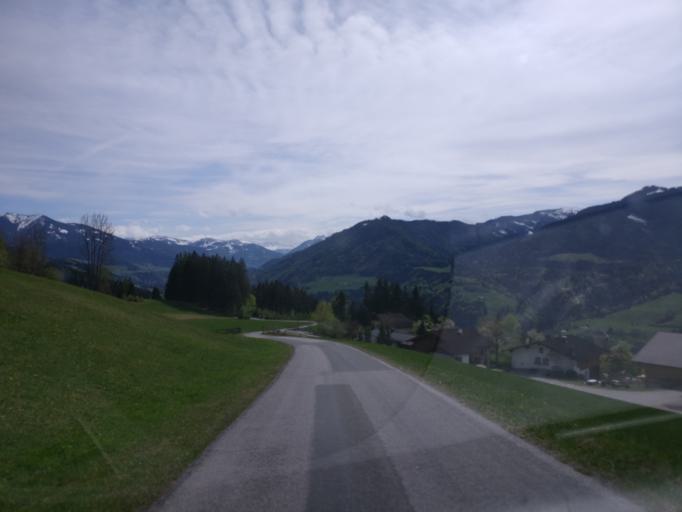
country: AT
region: Salzburg
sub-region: Politischer Bezirk Sankt Johann im Pongau
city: Pfarrwerfen
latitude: 47.4786
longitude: 13.2057
